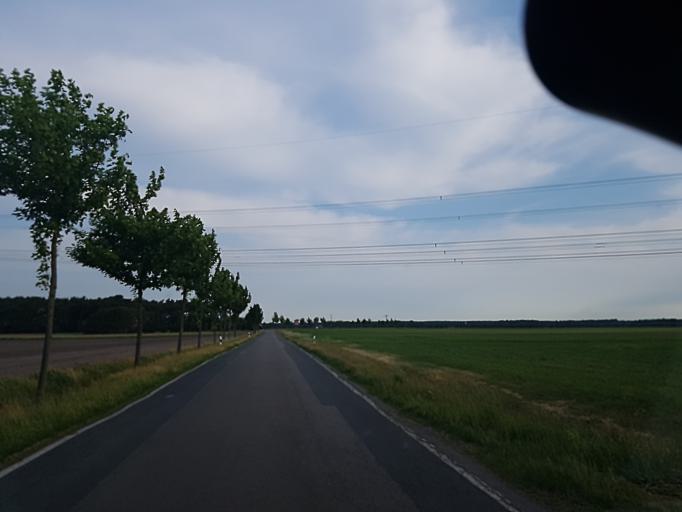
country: DE
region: Saxony-Anhalt
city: Jessen
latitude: 51.8233
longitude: 12.9482
